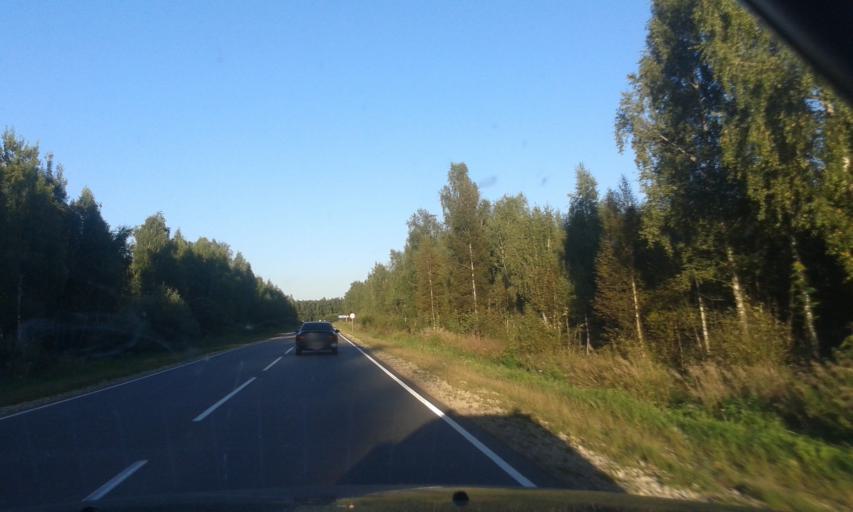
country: RU
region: Tula
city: Krapivna
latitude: 54.1372
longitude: 37.2720
